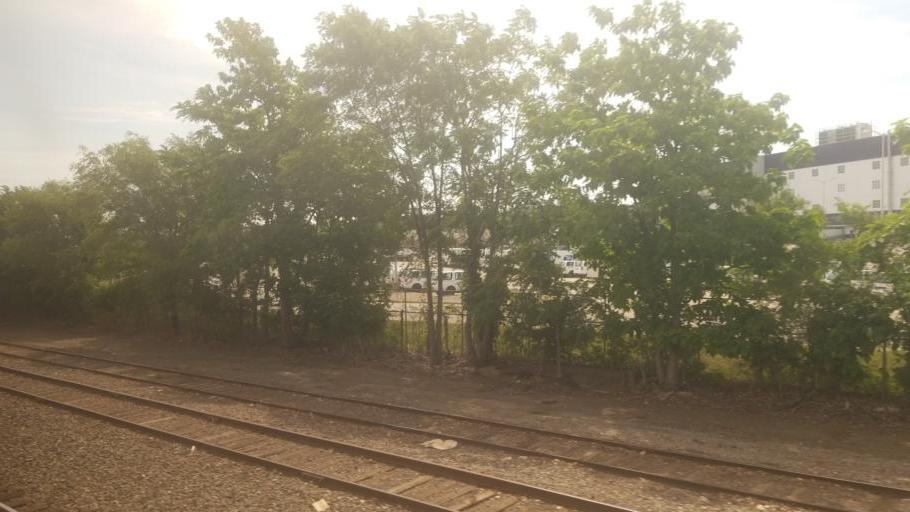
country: US
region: Missouri
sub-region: Jackson County
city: Kansas City
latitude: 39.0934
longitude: -94.5413
